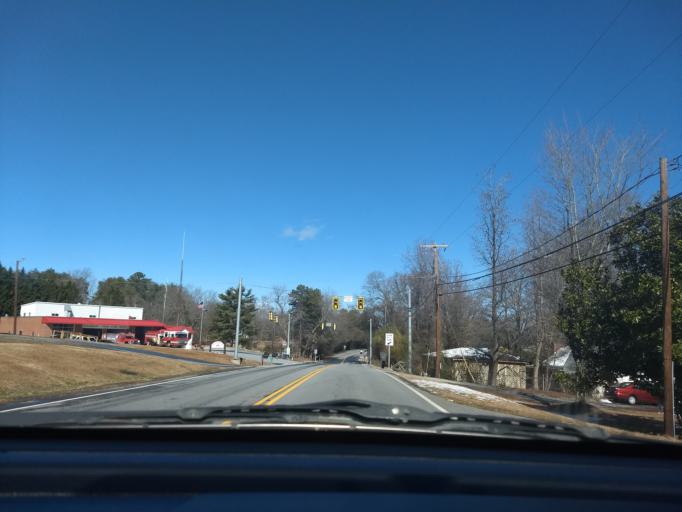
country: US
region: South Carolina
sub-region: Greenville County
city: Wade Hampton
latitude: 34.9118
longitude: -82.3725
